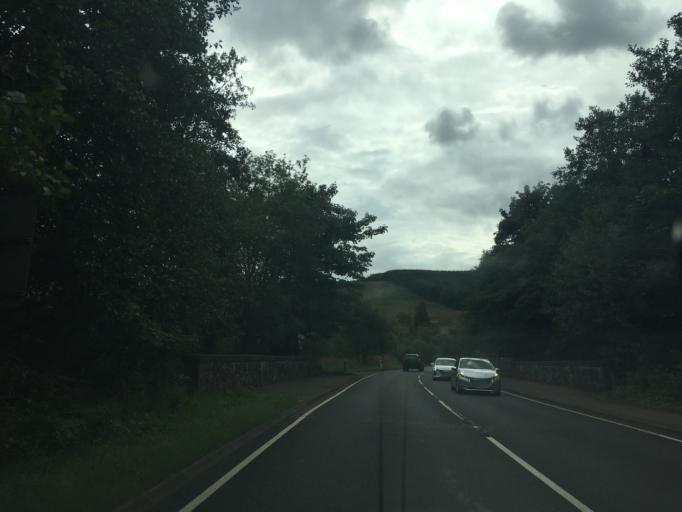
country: GB
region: Scotland
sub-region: Stirling
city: Callander
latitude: 56.3790
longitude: -4.2856
